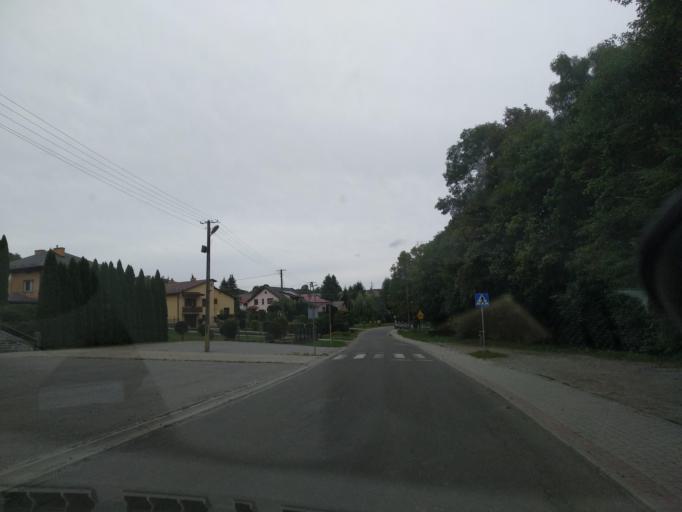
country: PL
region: Subcarpathian Voivodeship
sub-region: Powiat krosnienski
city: Iwonicz-Zdroj
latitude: 49.5790
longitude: 21.7522
